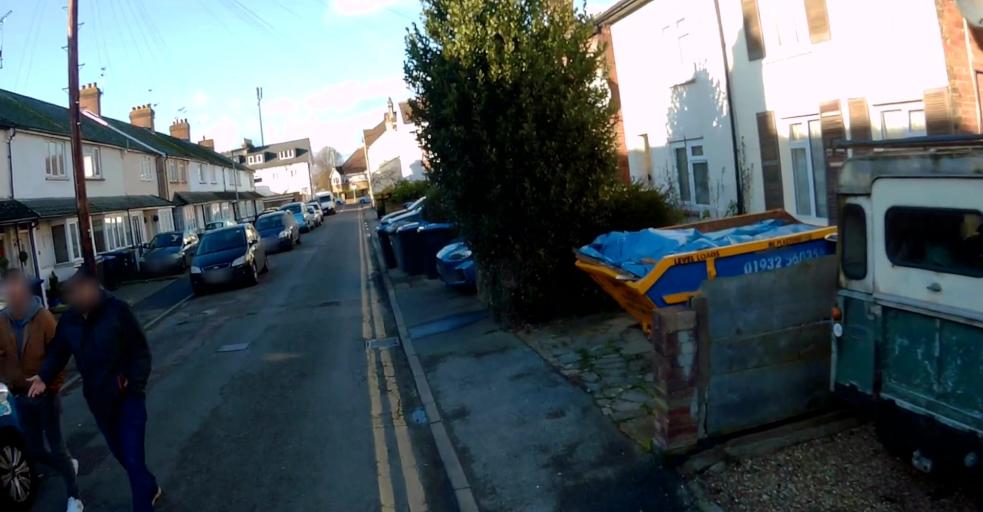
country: GB
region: England
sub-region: Surrey
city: Addlestone
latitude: 51.3725
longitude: -0.4825
